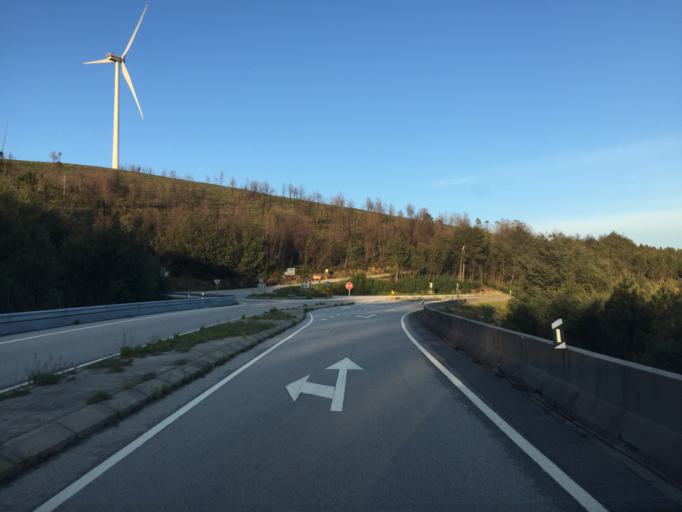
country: PT
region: Coimbra
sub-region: Pampilhosa da Serra
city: Pampilhosa da Serra
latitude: 40.1106
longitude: -8.0170
